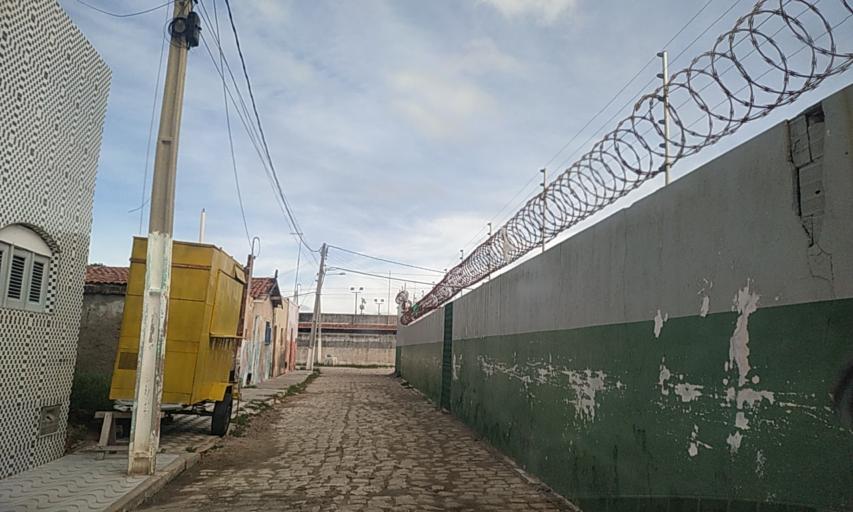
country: BR
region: Rio Grande do Norte
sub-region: Areia Branca
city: Areia Branca
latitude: -4.9551
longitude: -37.1289
